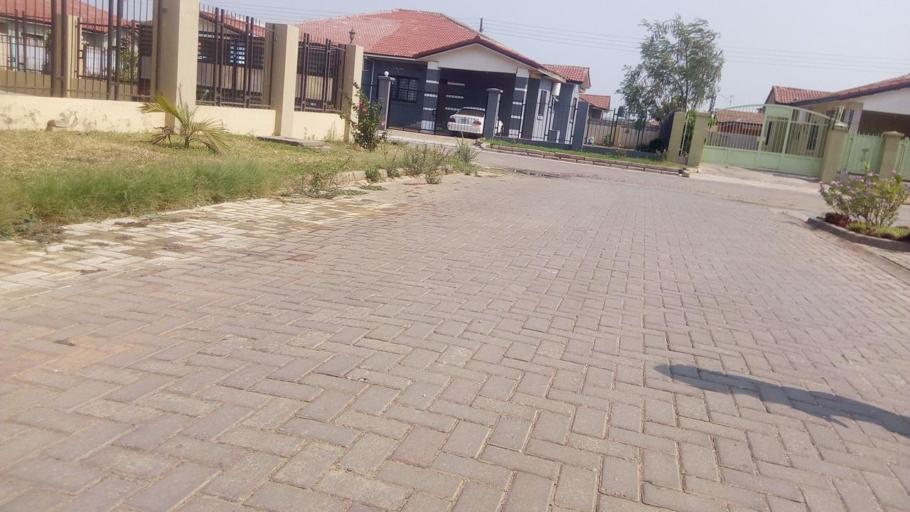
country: ZM
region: Lusaka
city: Lusaka
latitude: -15.3599
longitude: 28.2822
